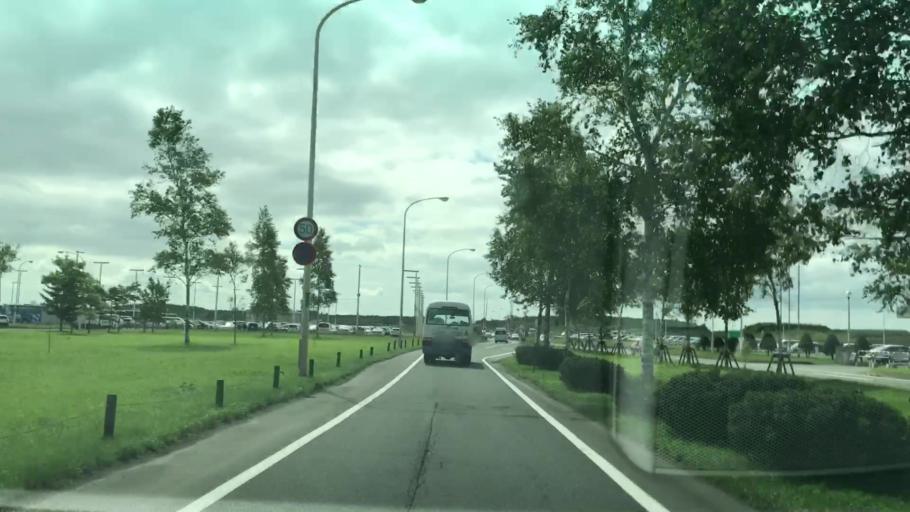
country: JP
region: Hokkaido
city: Chitose
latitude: 42.7824
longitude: 141.6777
